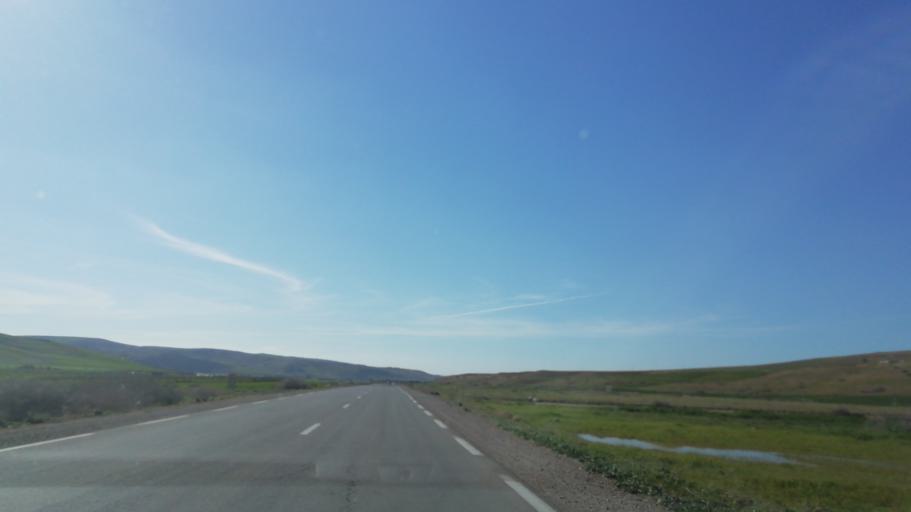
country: DZ
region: Mascara
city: Oued el Abtal
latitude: 35.4498
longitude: 0.8006
